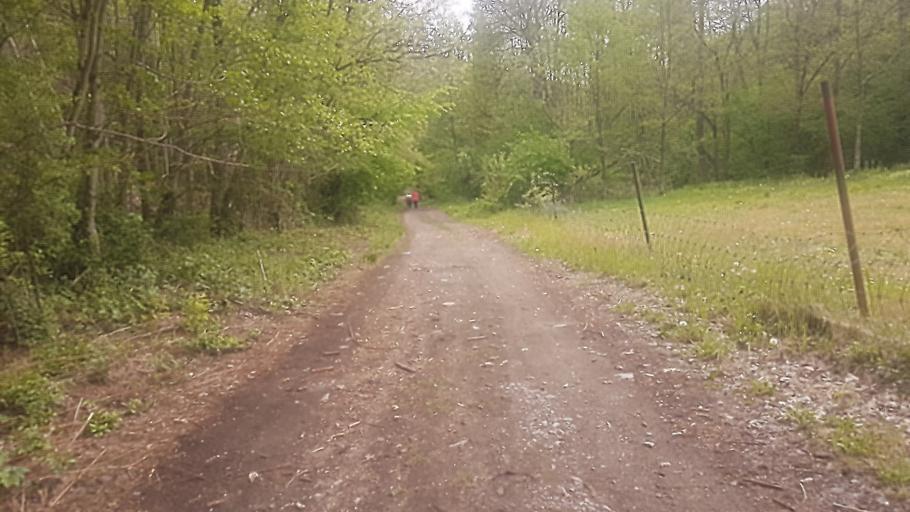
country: FR
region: Champagne-Ardenne
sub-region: Departement des Ardennes
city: Haybes
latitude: 50.0661
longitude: 4.6162
